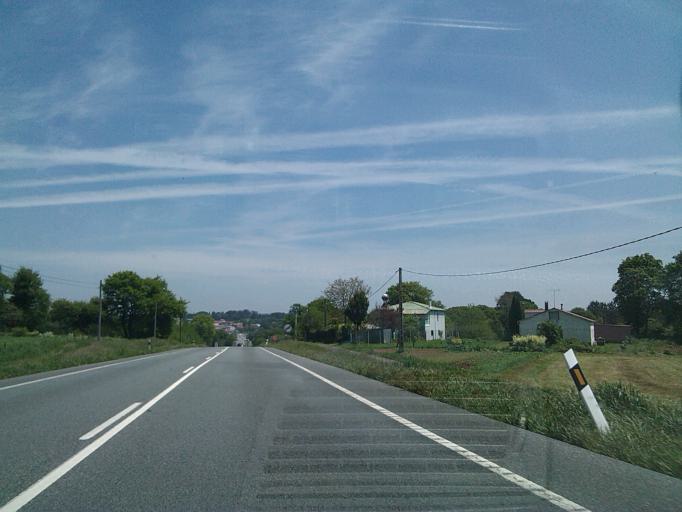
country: ES
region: Galicia
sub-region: Provincia da Coruna
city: Curtis
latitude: 43.1292
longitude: -8.0506
